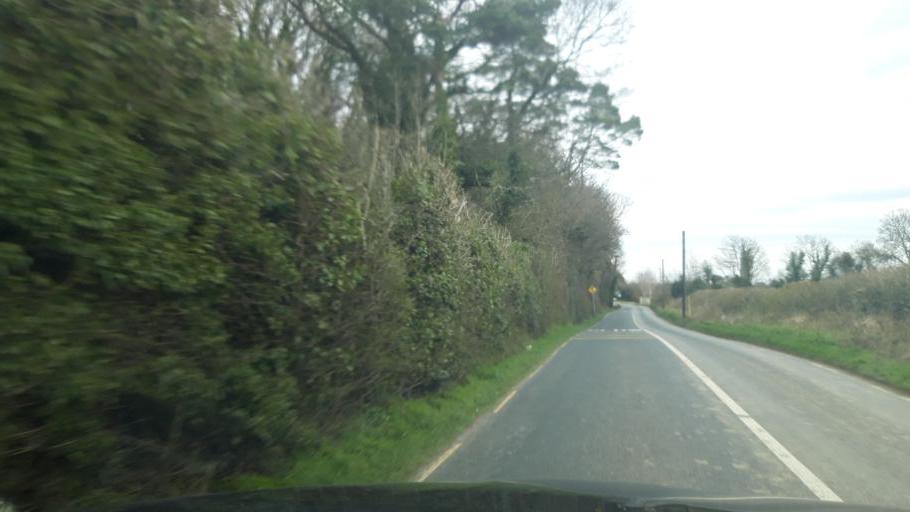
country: IE
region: Leinster
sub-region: Kildare
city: Maynooth
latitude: 53.3540
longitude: -6.6193
